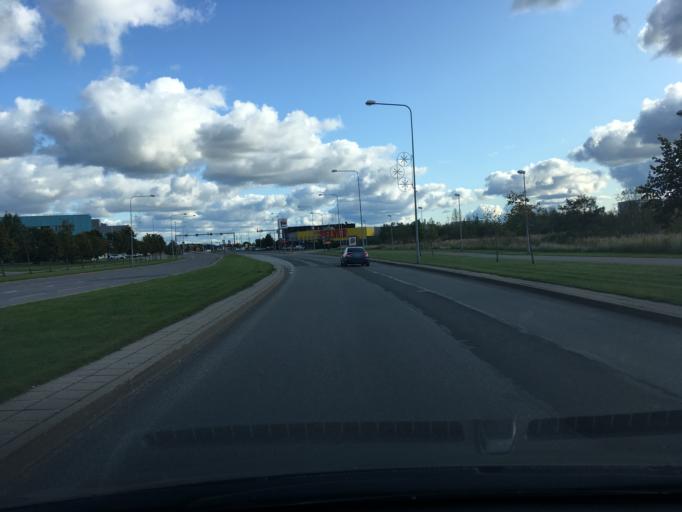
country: EE
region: Harju
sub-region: Tallinna linn
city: Kose
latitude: 59.4411
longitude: 24.8674
